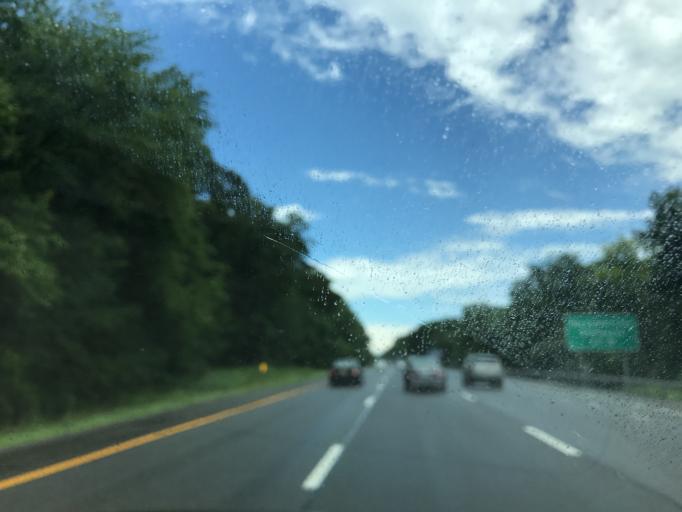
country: US
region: New York
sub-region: Saratoga County
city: Country Knolls
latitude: 42.8448
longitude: -73.7720
